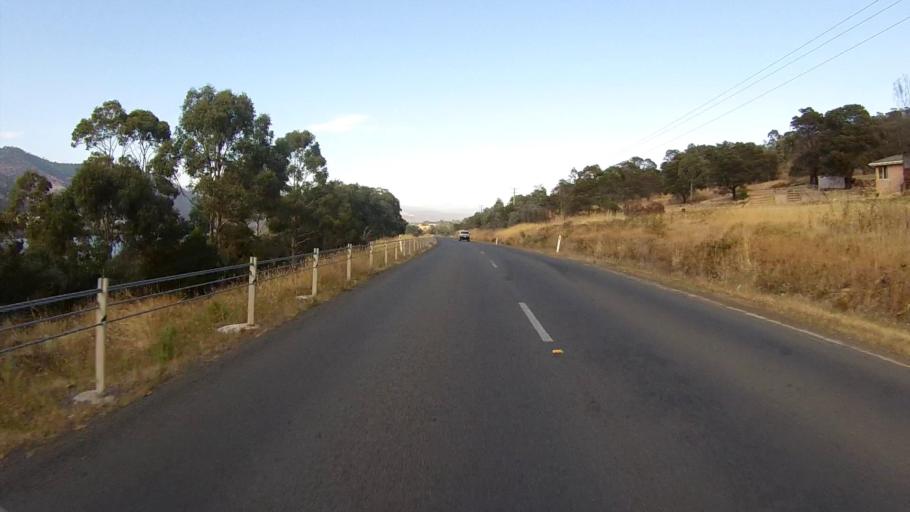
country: AU
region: Tasmania
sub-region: Glenorchy
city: Granton
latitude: -42.7525
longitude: 147.1484
